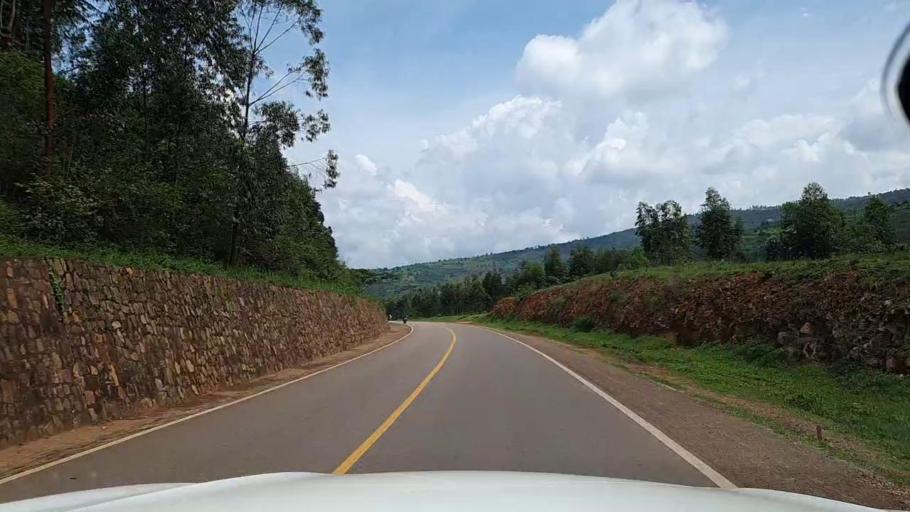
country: RW
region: Kigali
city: Kigali
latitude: -1.8566
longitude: 30.0965
